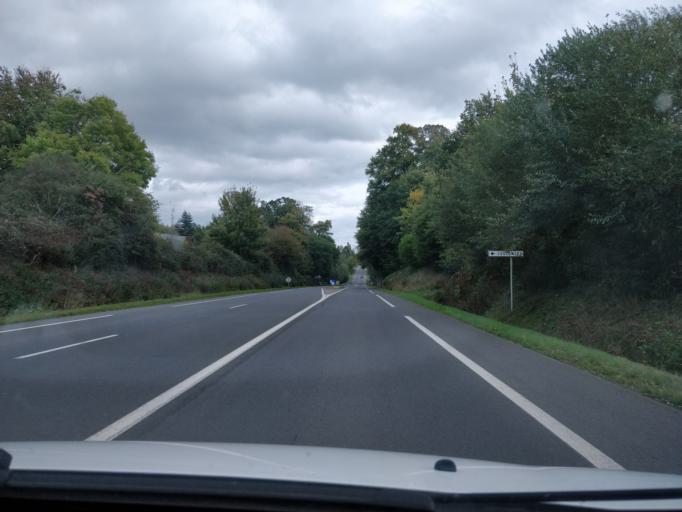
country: FR
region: Lower Normandy
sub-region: Departement du Calvados
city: Vire
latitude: 48.8412
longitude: -0.9445
